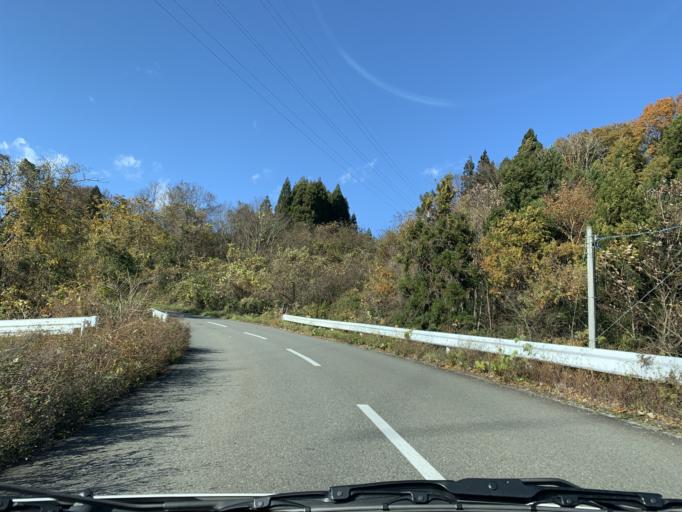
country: JP
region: Iwate
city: Mizusawa
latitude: 39.0925
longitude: 141.1248
